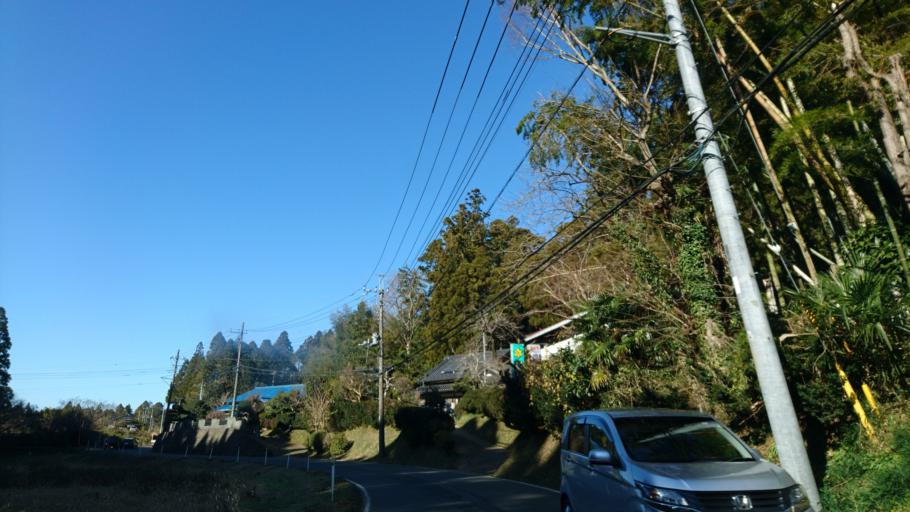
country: JP
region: Chiba
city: Yachimata
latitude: 35.6142
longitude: 140.3437
